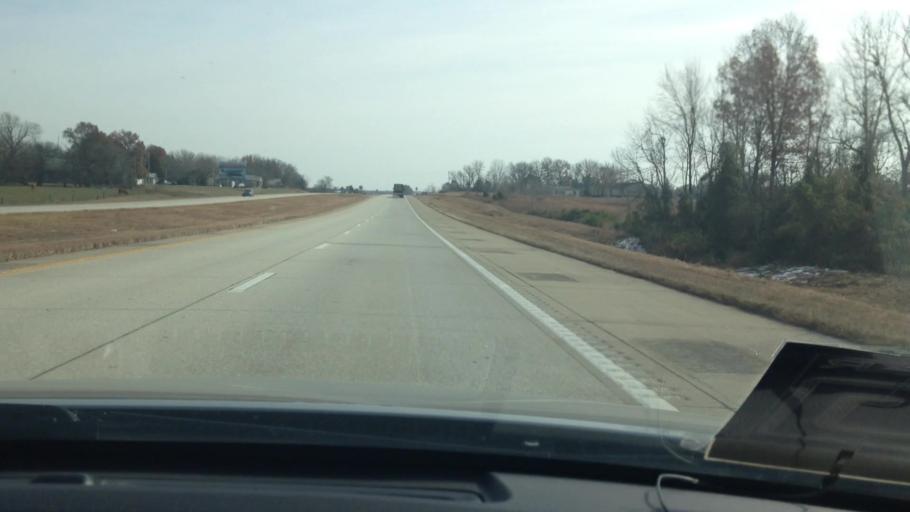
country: US
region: Missouri
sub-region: Henry County
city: Clinton
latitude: 38.4365
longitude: -93.9399
